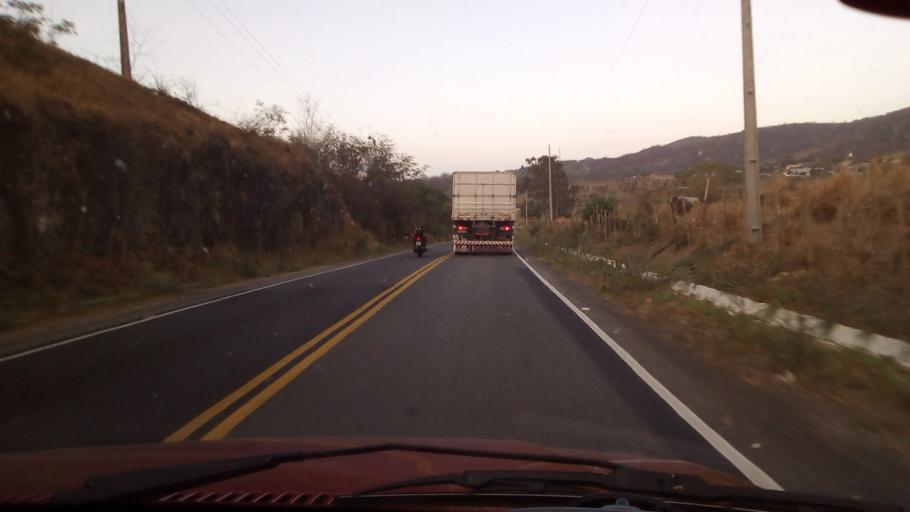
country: BR
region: Paraiba
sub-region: Bananeiras
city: Solanea
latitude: -6.7254
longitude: -35.5523
